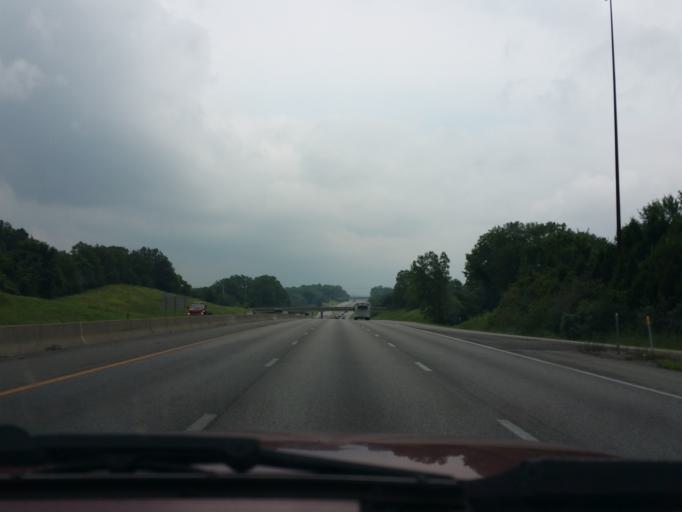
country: US
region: Kansas
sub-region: Johnson County
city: Shawnee
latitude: 39.1061
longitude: -94.7338
